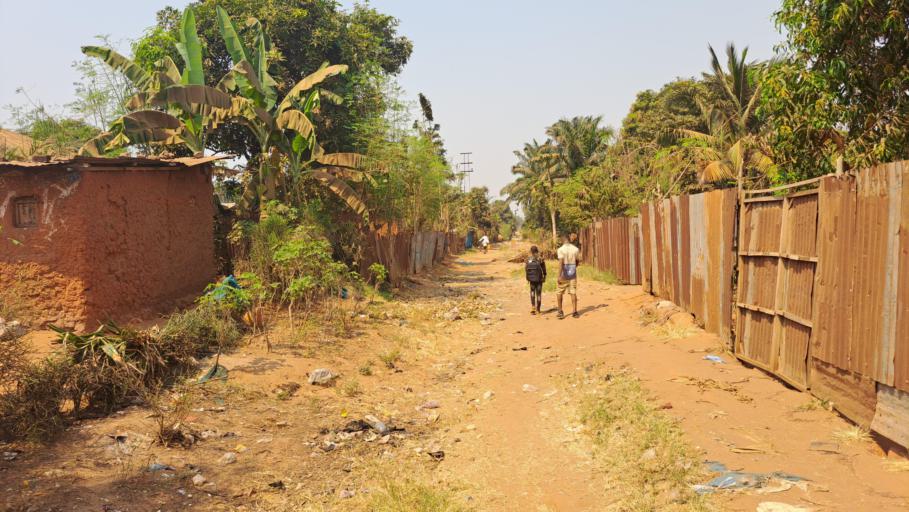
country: CD
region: Kasai-Oriental
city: Mbuji-Mayi
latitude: -6.1233
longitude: 23.6086
